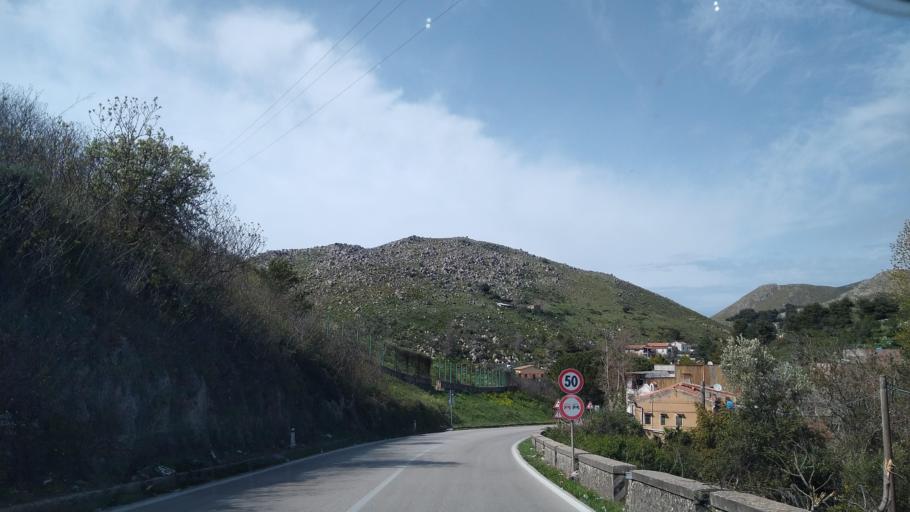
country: IT
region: Sicily
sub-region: Palermo
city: Pioppo
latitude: 38.0466
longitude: 13.1979
